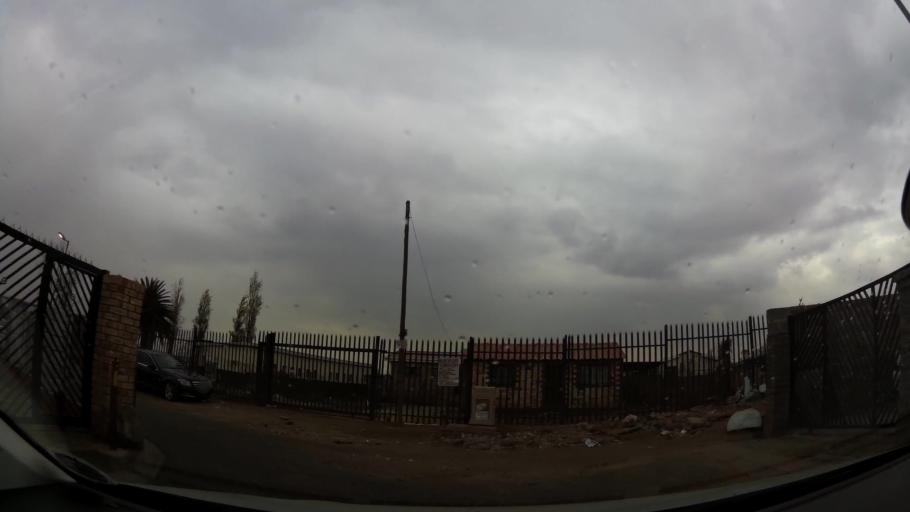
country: ZA
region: Gauteng
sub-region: City of Johannesburg Metropolitan Municipality
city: Soweto
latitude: -26.2513
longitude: 27.8656
